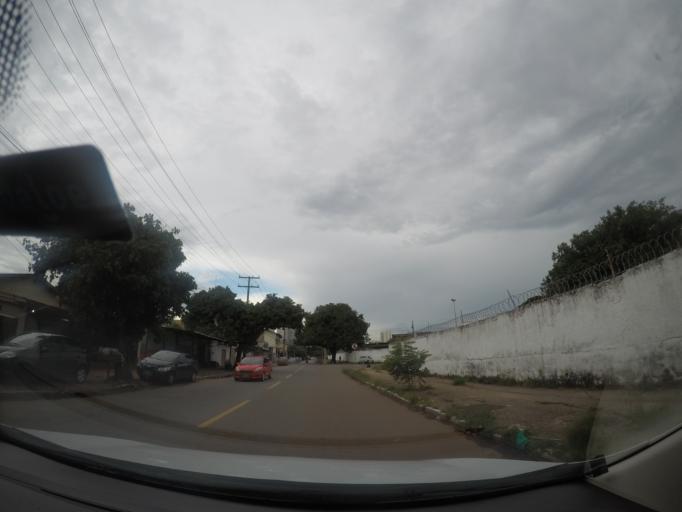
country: BR
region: Goias
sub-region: Goiania
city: Goiania
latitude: -16.6563
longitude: -49.2500
